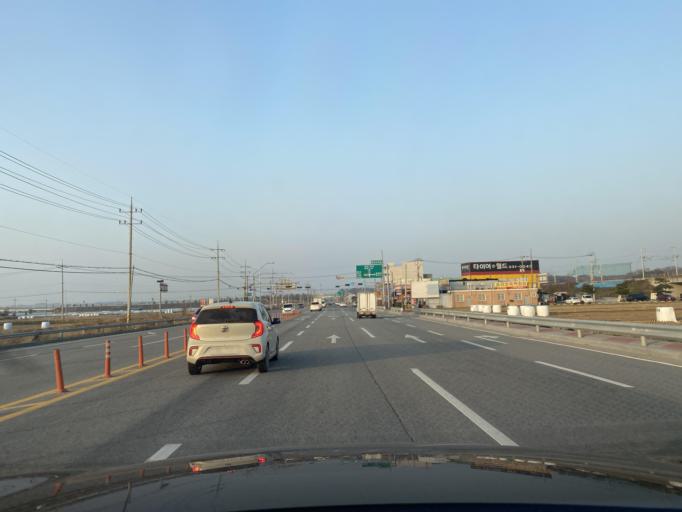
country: KR
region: Chungcheongnam-do
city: Yesan
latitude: 36.6975
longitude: 126.8288
